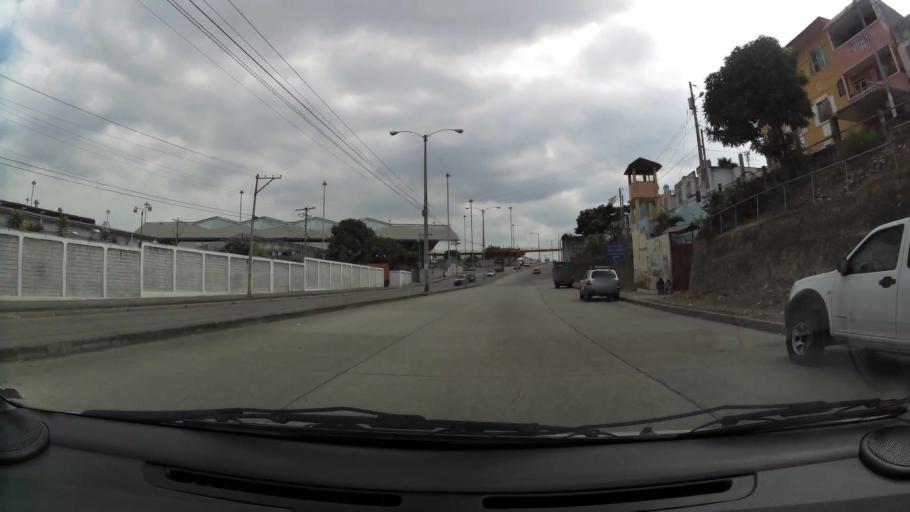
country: EC
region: Guayas
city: Santa Lucia
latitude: -2.0918
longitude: -79.9388
